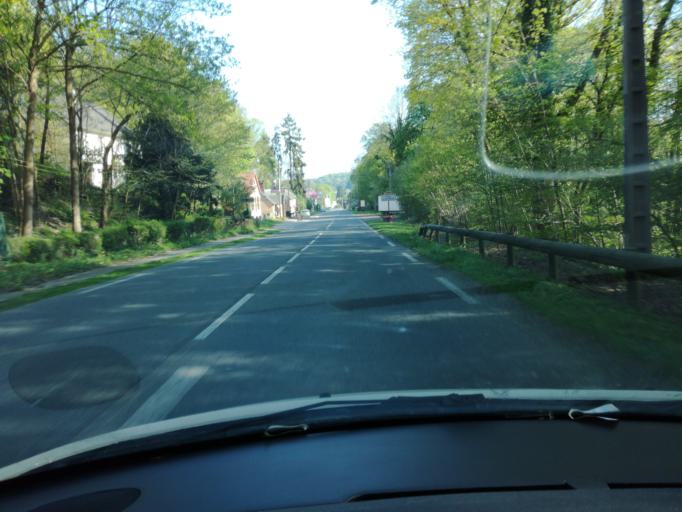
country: FR
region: Picardie
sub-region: Departement de la Somme
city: Poix-de-Picardie
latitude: 49.7805
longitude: 1.9832
